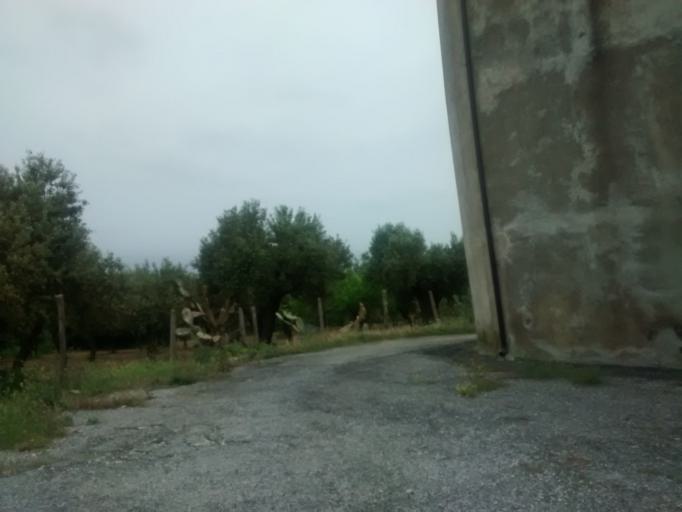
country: IT
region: Calabria
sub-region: Provincia di Catanzaro
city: Maida
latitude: 38.8981
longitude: 16.3906
